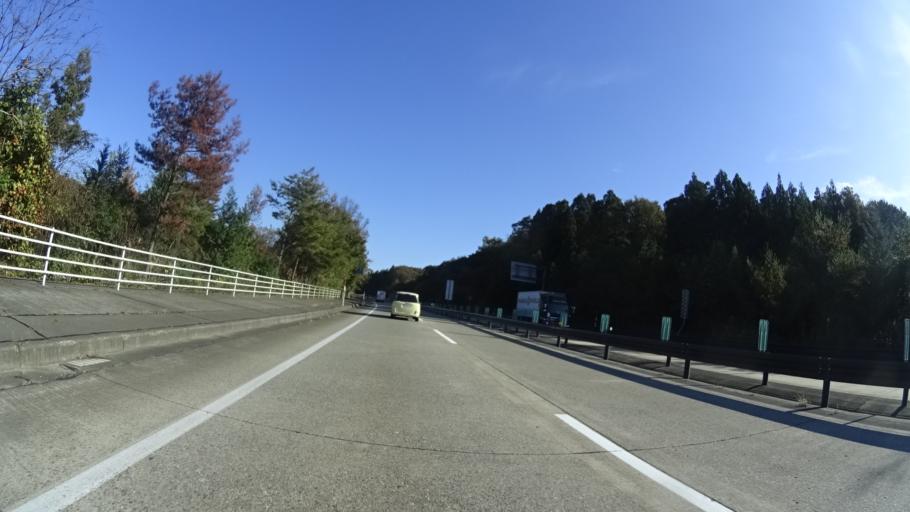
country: JP
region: Ishikawa
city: Komatsu
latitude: 36.3439
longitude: 136.4469
